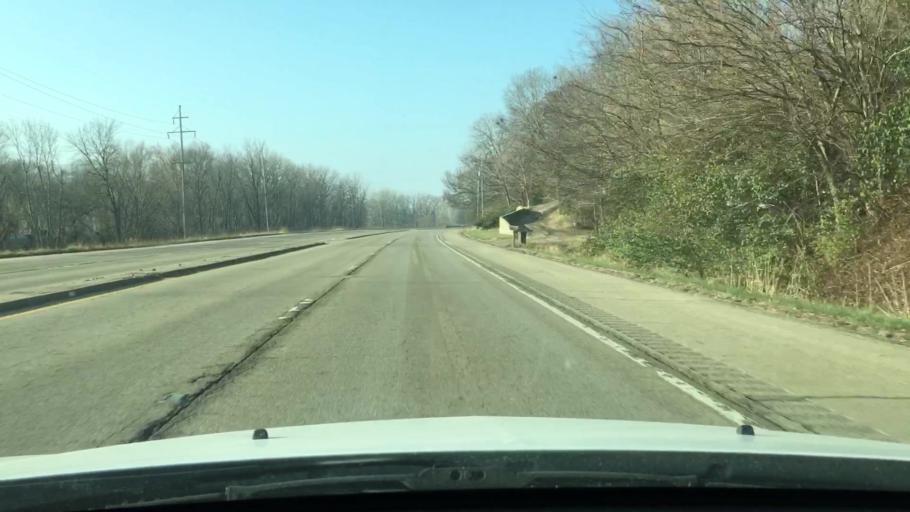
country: US
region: Illinois
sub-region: Tazewell County
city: Pekin
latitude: 40.5850
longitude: -89.6860
